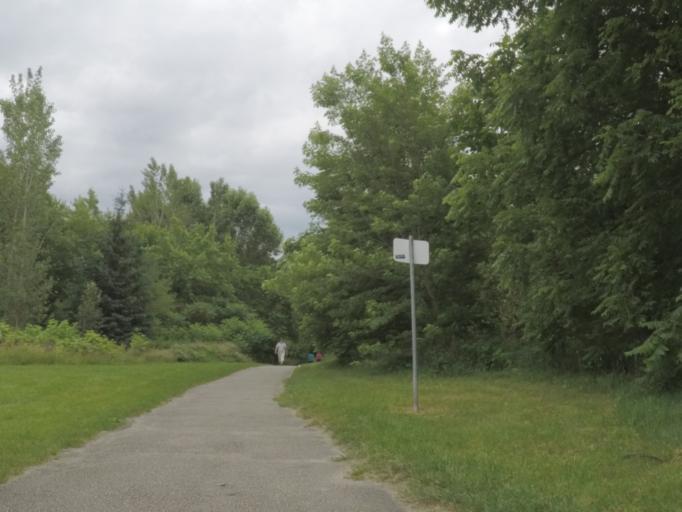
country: CA
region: Ontario
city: Etobicoke
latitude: 43.6598
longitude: -79.5581
